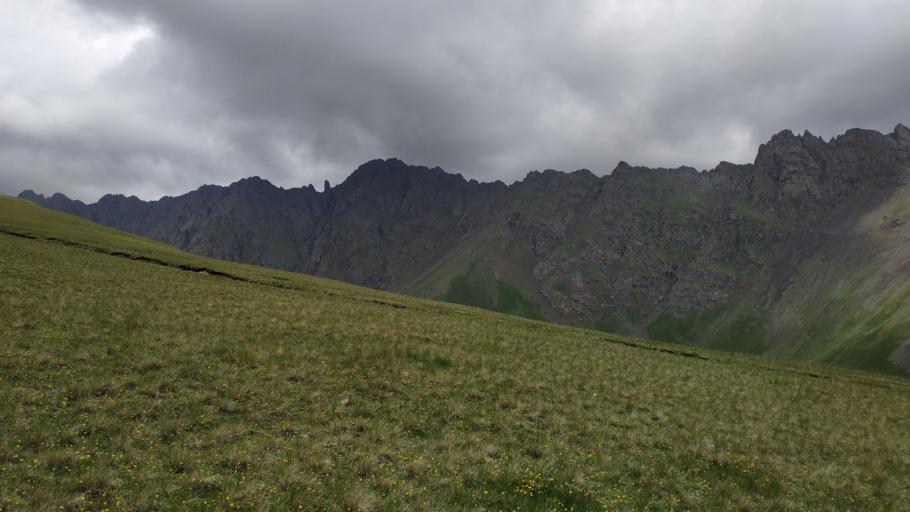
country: RU
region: Kabardino-Balkariya
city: Terskol
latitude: 43.4287
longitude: 42.5021
